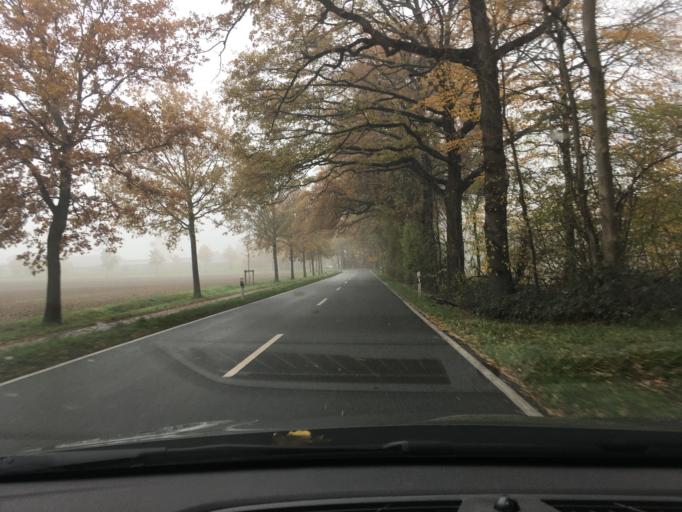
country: DE
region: North Rhine-Westphalia
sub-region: Regierungsbezirk Munster
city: Ahaus
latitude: 52.1183
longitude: 6.9203
